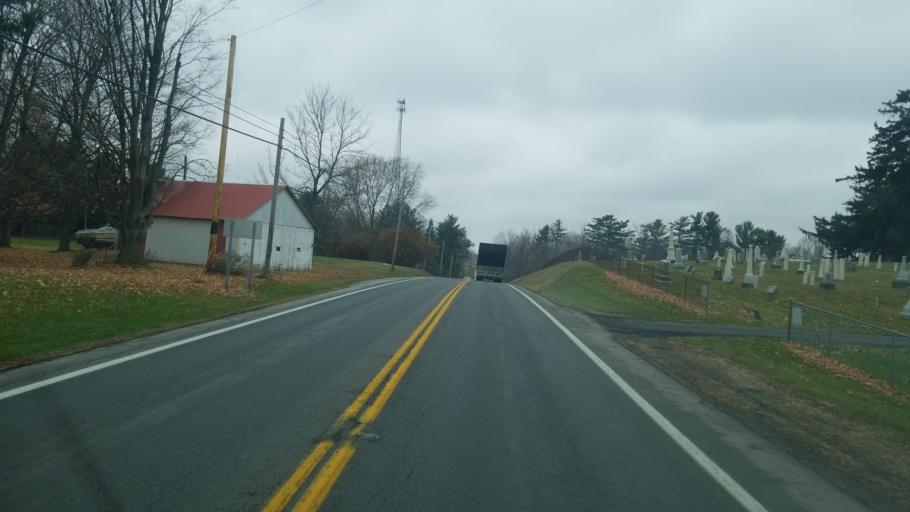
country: US
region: Ohio
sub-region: Huron County
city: Greenwich
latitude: 41.0974
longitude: -82.4907
